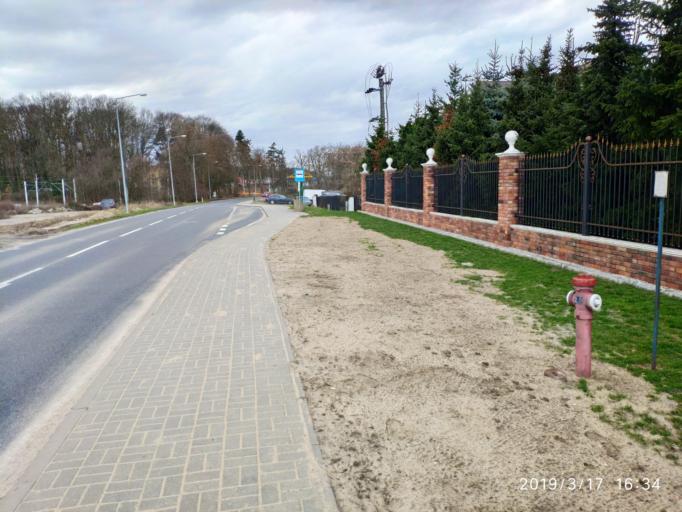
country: PL
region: Lubusz
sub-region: Zielona Gora
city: Zielona Gora
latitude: 51.9339
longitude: 15.5950
